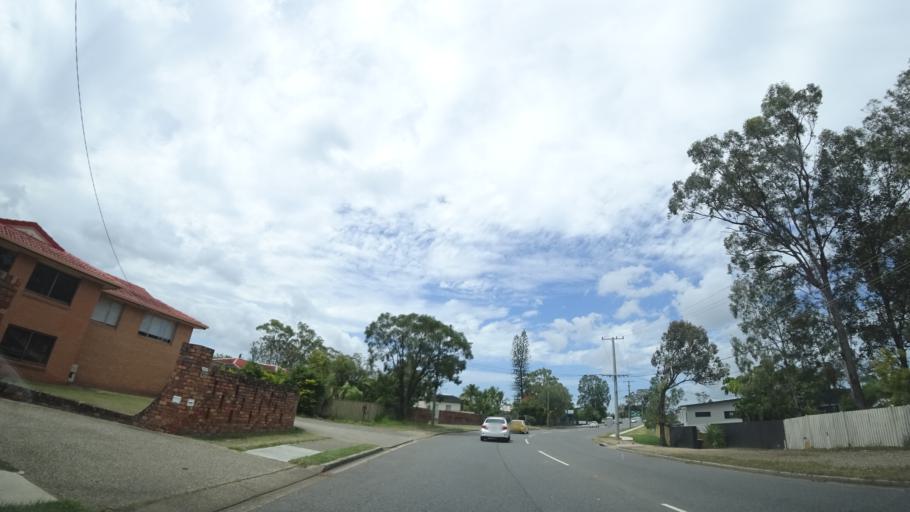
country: AU
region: Queensland
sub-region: Brisbane
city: Everton Park
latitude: -27.3876
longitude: 152.9813
